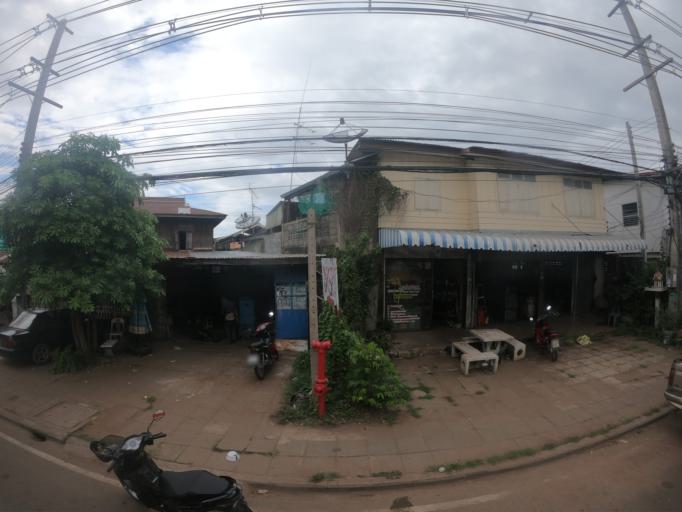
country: TH
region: Buriram
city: Prakhon Chai
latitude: 14.6107
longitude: 103.0794
